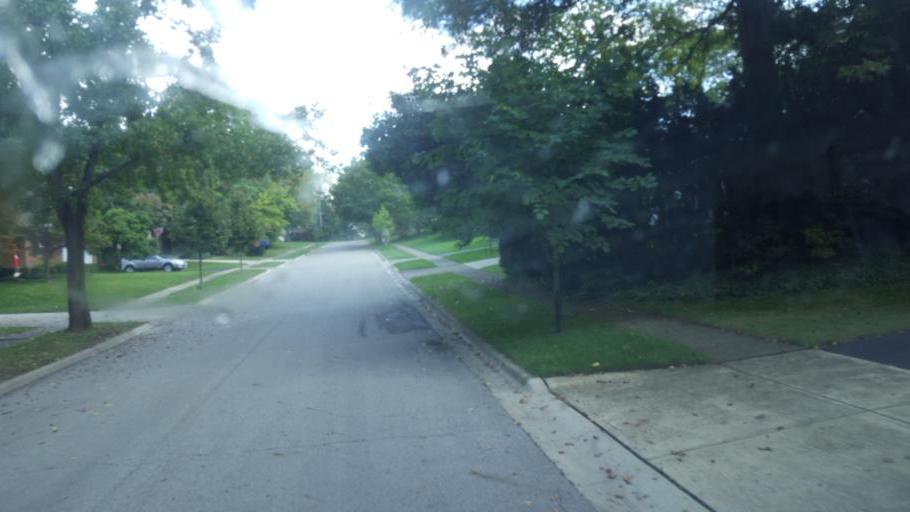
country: US
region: Ohio
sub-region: Franklin County
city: Worthington
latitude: 40.1002
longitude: -83.0323
